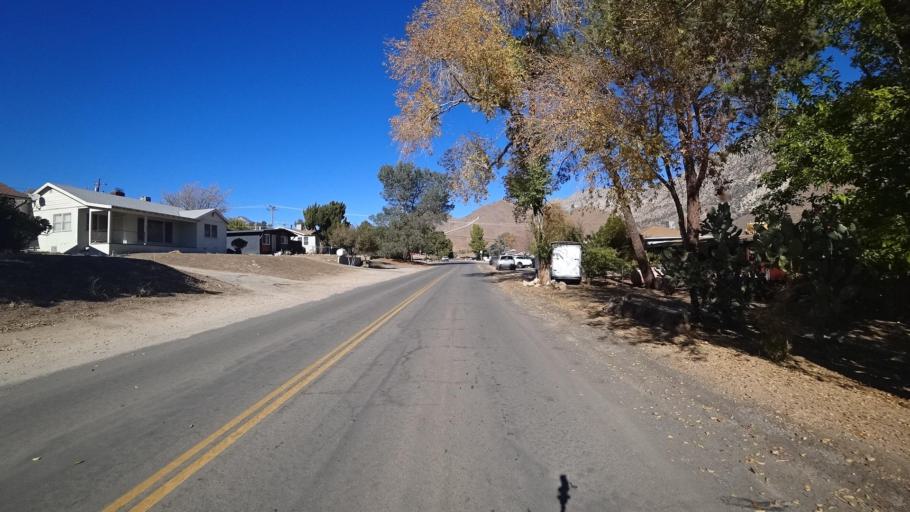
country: US
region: California
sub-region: Kern County
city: Kernville
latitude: 35.7619
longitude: -118.4314
